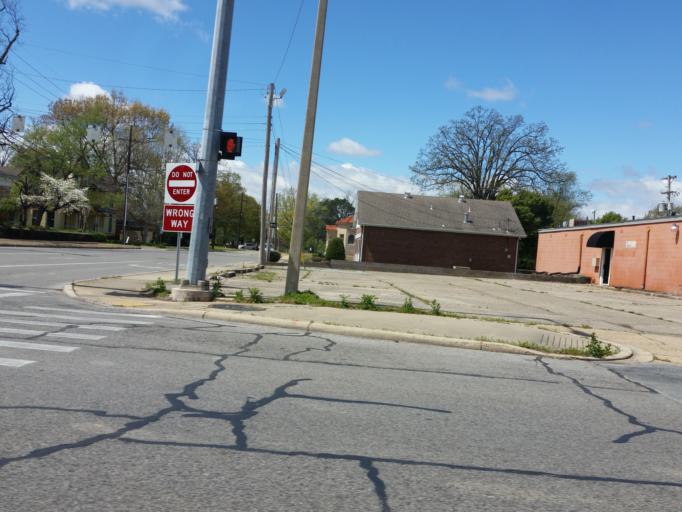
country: US
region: Arkansas
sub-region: Craighead County
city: Jonesboro
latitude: 35.8339
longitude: -90.7051
